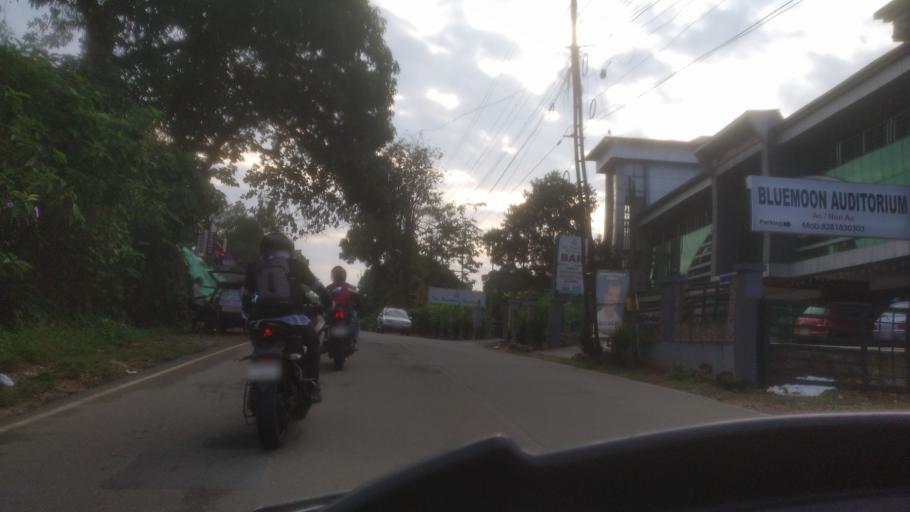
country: IN
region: Kerala
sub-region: Ernakulam
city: Kotamangalam
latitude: 10.0678
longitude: 76.6243
